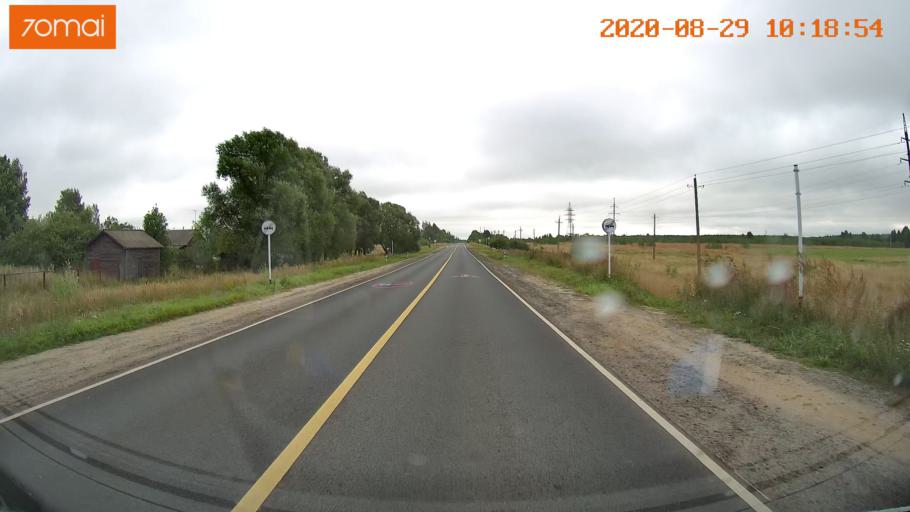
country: RU
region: Ivanovo
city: Yur'yevets
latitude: 57.3298
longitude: 42.8489
